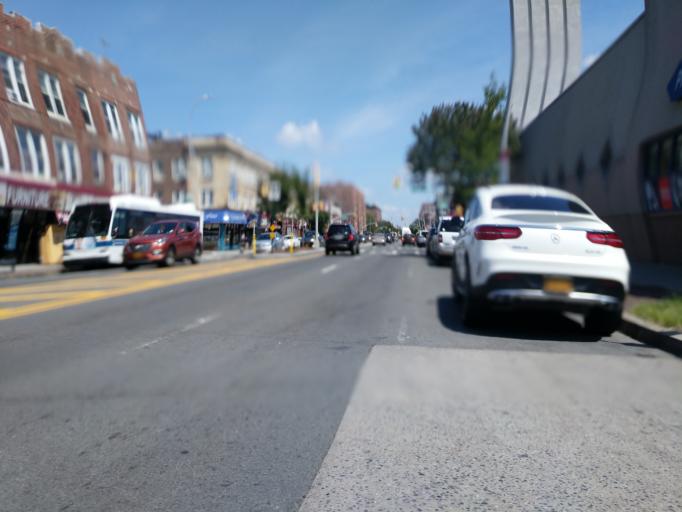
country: US
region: New York
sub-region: Queens County
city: Long Island City
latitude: 40.7558
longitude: -73.8823
